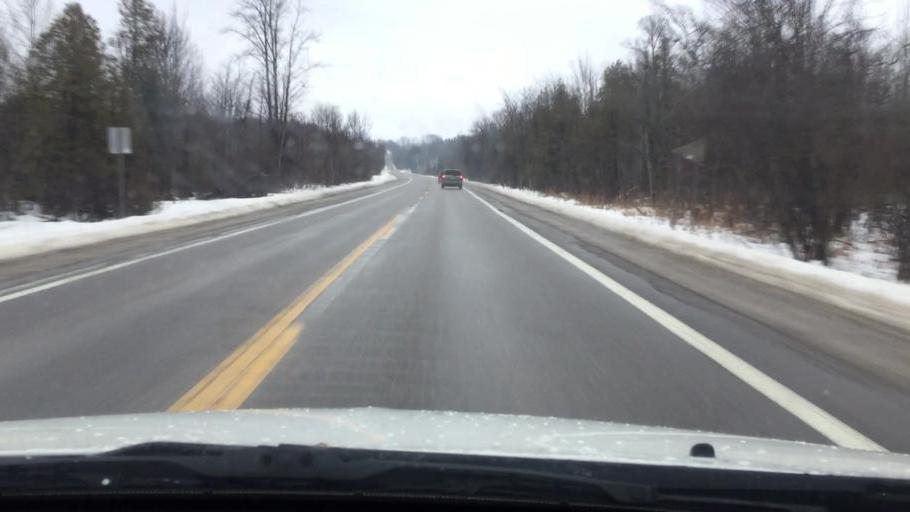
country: US
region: Michigan
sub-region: Charlevoix County
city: East Jordan
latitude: 45.2367
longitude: -85.1815
